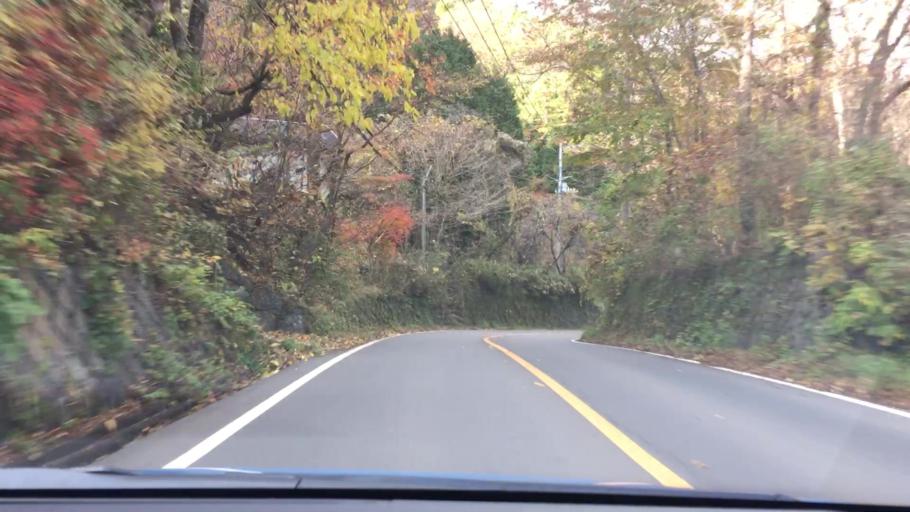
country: JP
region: Yamanashi
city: Otsuki
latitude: 35.4773
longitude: 138.9517
